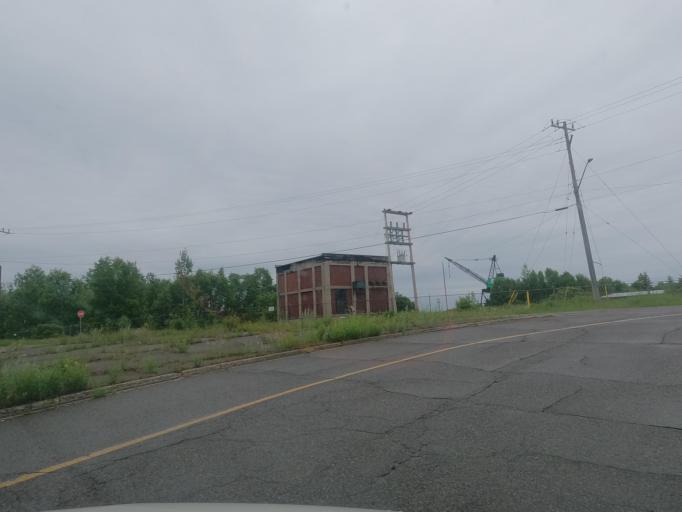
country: CA
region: Ontario
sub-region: Thunder Bay District
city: Thunder Bay
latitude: 48.4544
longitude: -89.1824
